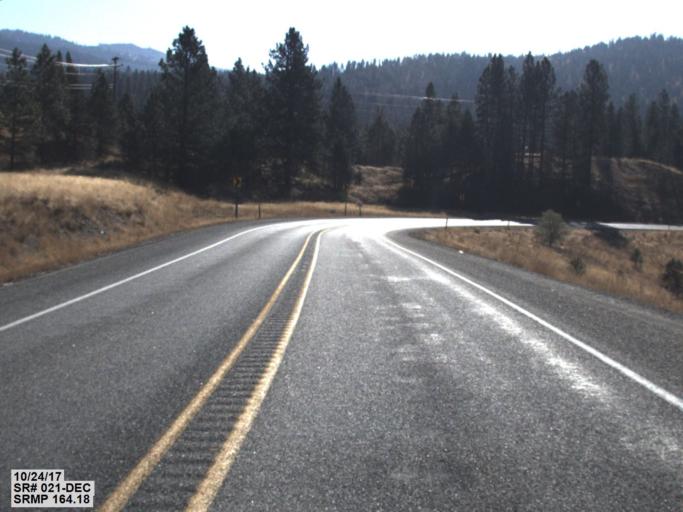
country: US
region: Washington
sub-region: Ferry County
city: Republic
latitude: 48.6627
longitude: -118.6660
